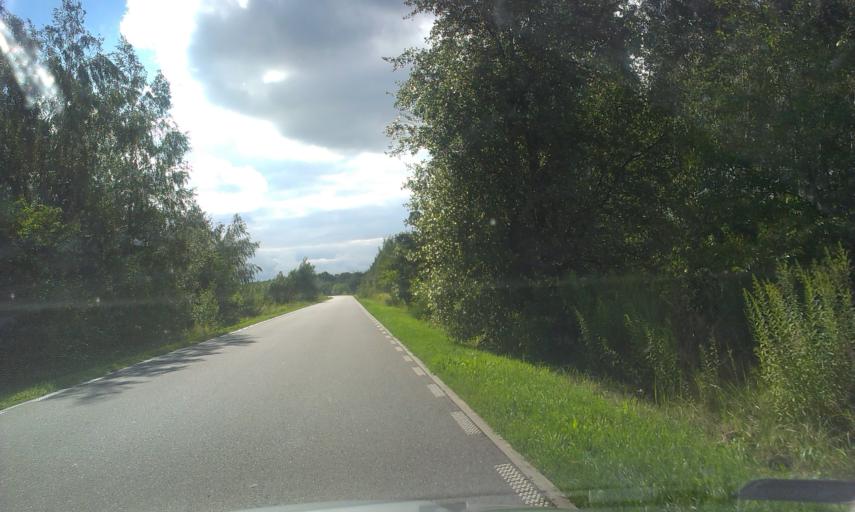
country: PL
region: Lodz Voivodeship
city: Zabia Wola
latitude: 51.9681
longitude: 20.6302
